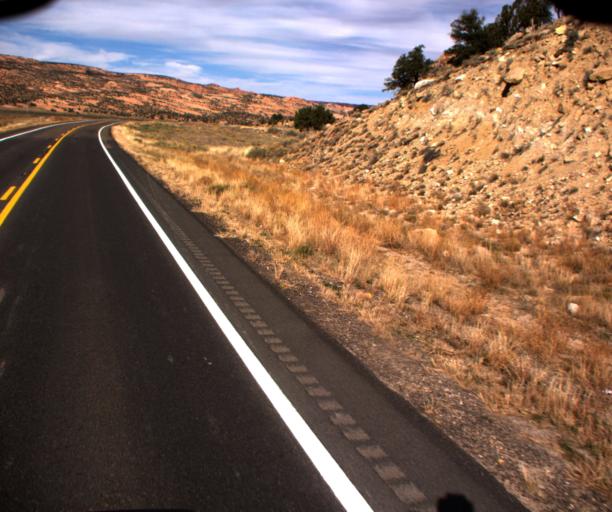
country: US
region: Arizona
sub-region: Navajo County
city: Kayenta
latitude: 36.6068
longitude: -110.4730
